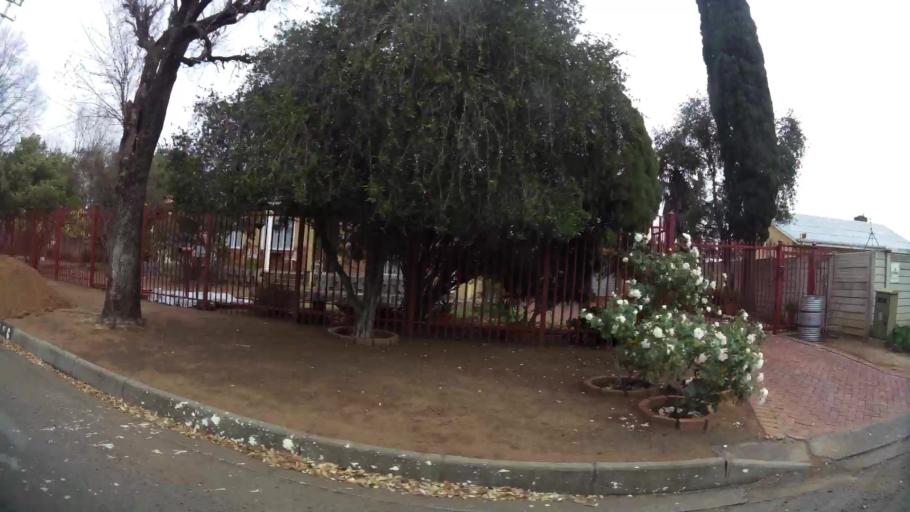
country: ZA
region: Orange Free State
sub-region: Mangaung Metropolitan Municipality
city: Bloemfontein
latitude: -29.1325
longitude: 26.1800
